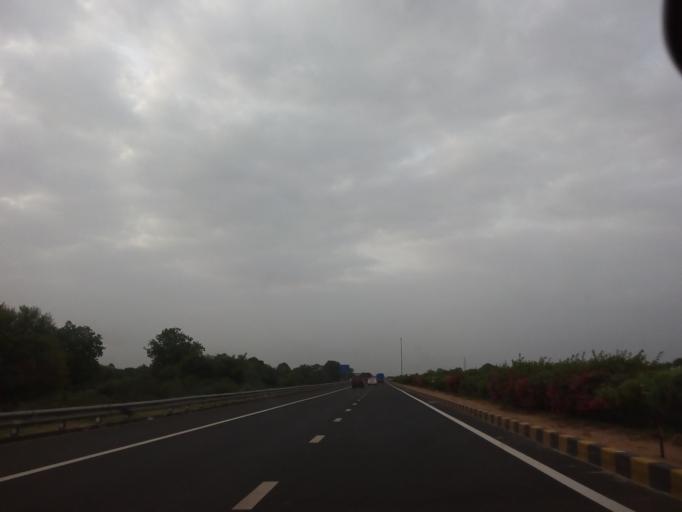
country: IN
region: Gujarat
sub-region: Kheda
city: Mahemdavad
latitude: 22.9155
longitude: 72.7604
